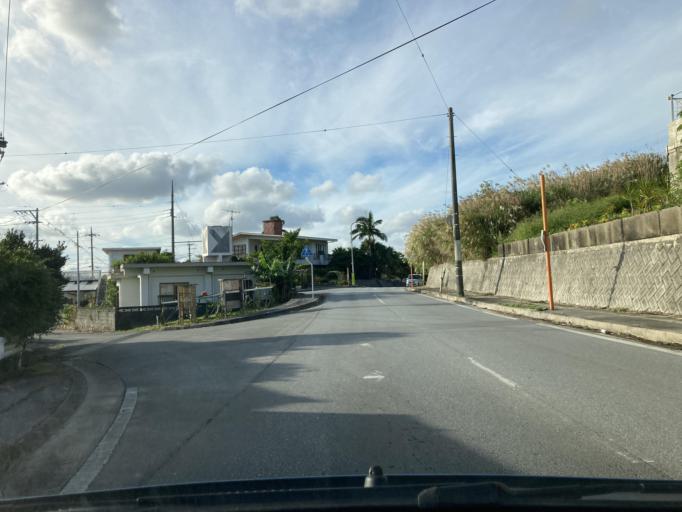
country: JP
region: Okinawa
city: Tomigusuku
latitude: 26.1583
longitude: 127.7379
